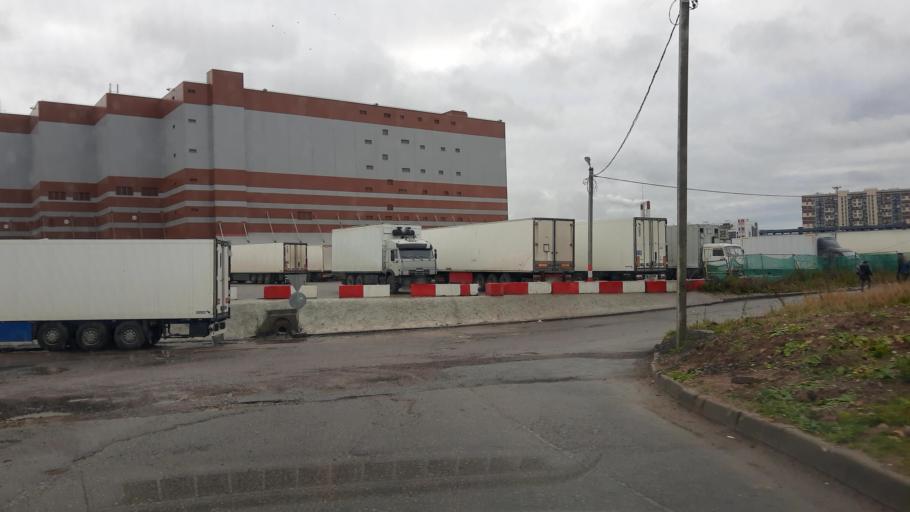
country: RU
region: Moskovskaya
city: Mosrentgen
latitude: 55.6002
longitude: 37.4567
